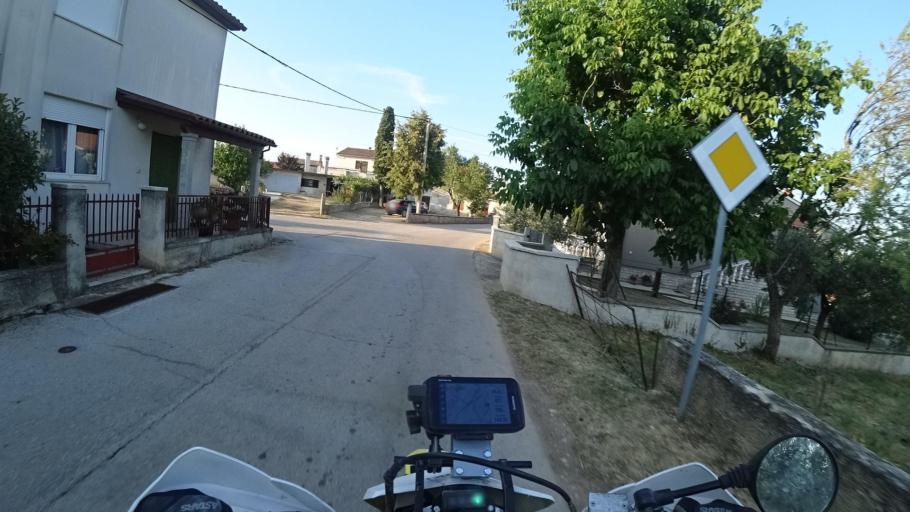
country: HR
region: Istarska
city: Marcana
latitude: 45.0038
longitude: 13.9153
